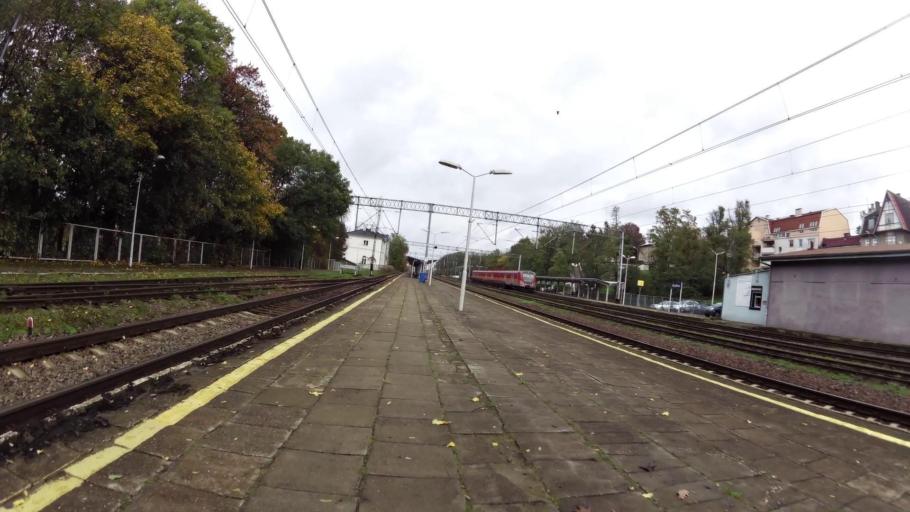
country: PL
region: West Pomeranian Voivodeship
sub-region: Powiat gryfinski
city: Gryfino
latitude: 53.2532
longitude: 14.4931
